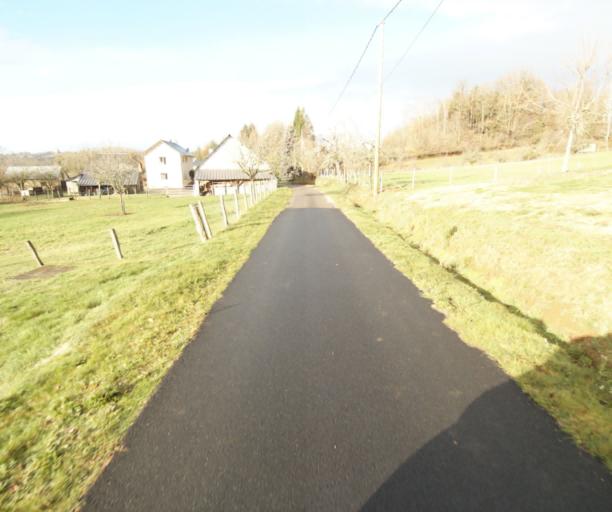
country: FR
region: Limousin
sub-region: Departement de la Correze
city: Saint-Mexant
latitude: 45.2766
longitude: 1.6050
